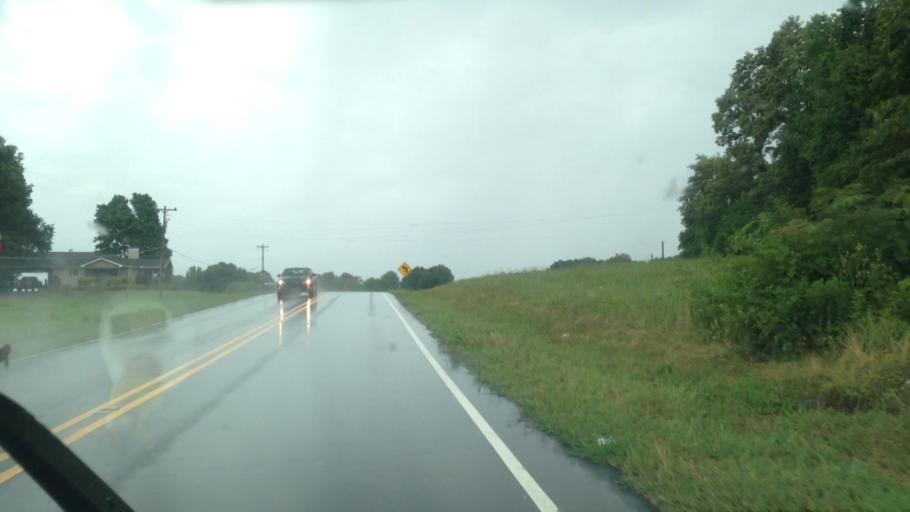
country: US
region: North Carolina
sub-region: Stokes County
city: Danbury
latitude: 36.4512
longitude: -80.1032
